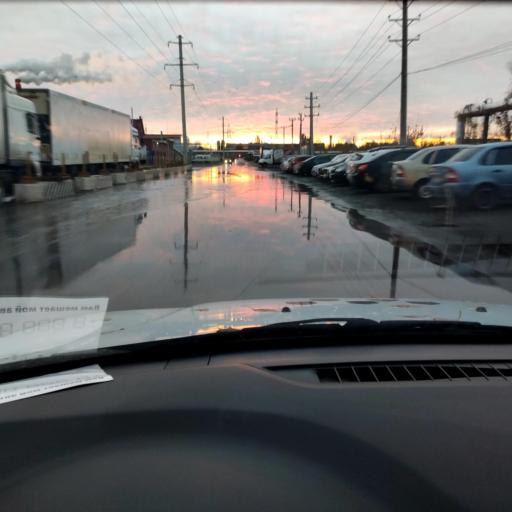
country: RU
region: Samara
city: Tol'yatti
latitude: 53.5464
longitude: 49.4368
